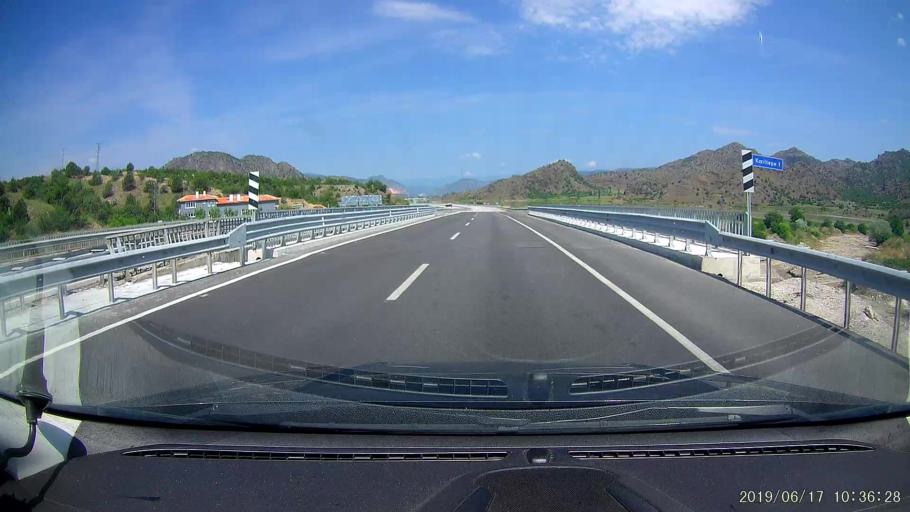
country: TR
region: Corum
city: Osmancik
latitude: 40.9795
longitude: 34.6805
